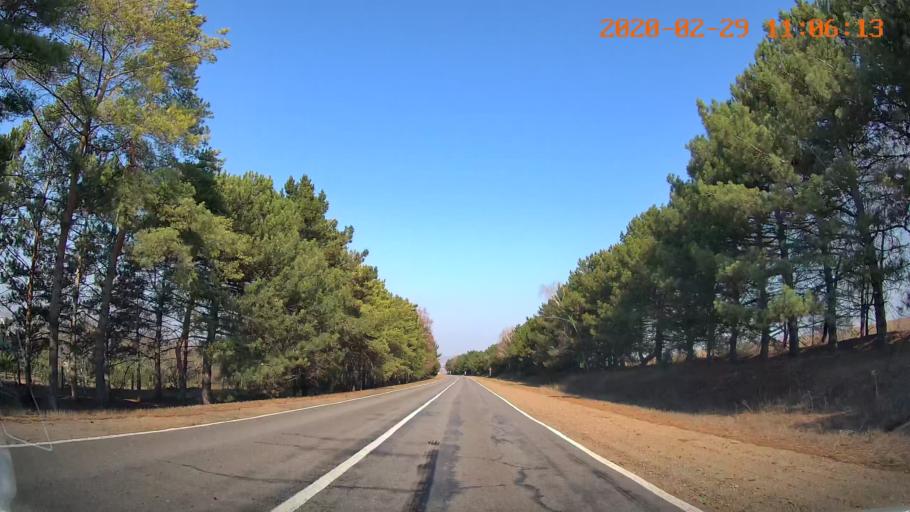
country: MD
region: Criuleni
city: Criuleni
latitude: 47.2120
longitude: 29.1891
